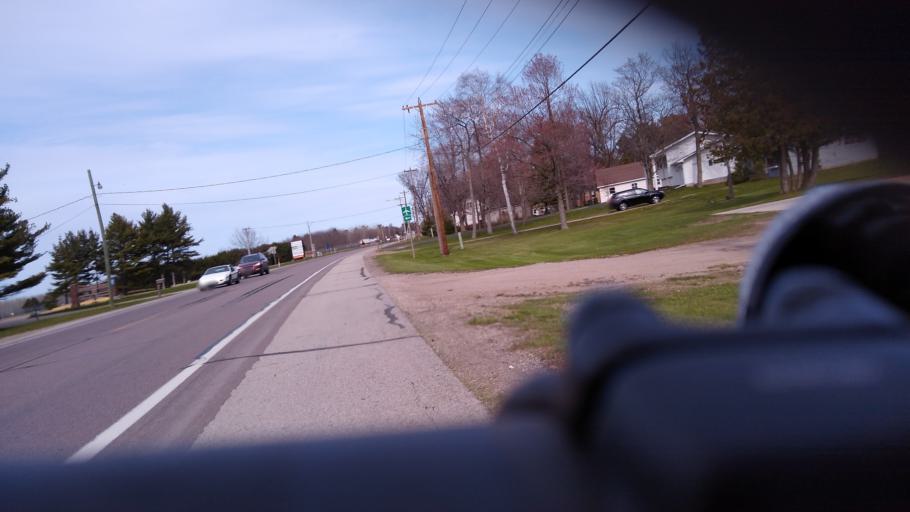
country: US
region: Michigan
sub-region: Delta County
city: Escanaba
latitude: 45.7128
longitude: -87.0903
